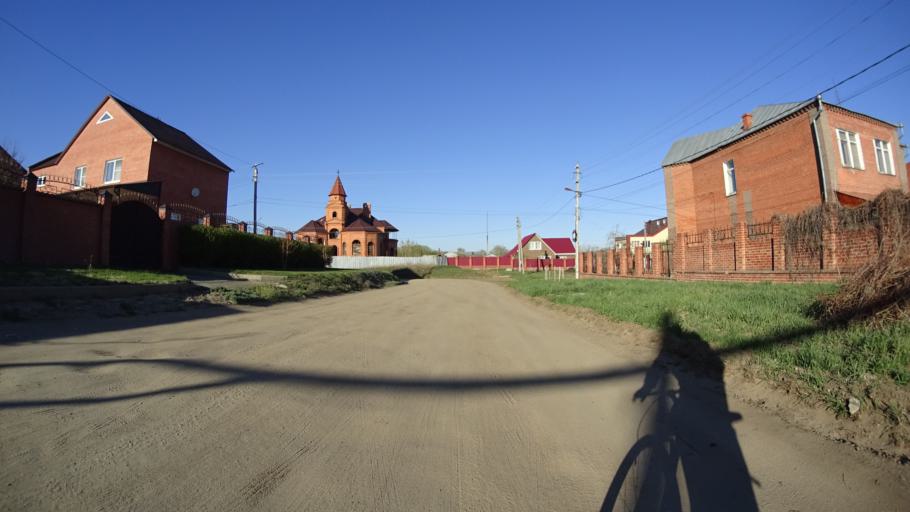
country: RU
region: Chelyabinsk
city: Troitsk
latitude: 54.0709
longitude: 61.5356
